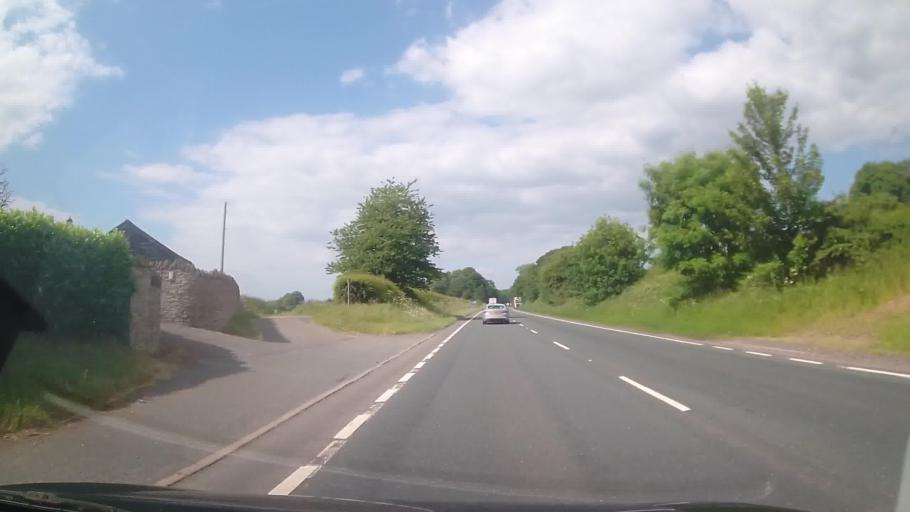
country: GB
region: England
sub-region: Shropshire
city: Ludlow
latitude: 52.3439
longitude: -2.7107
